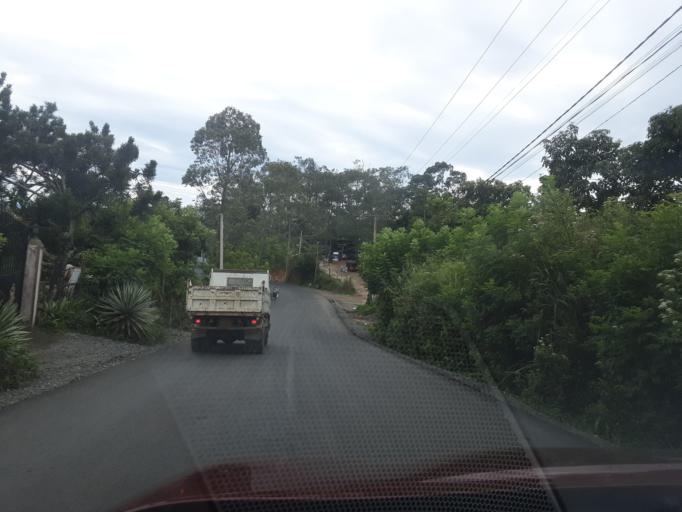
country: LK
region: Uva
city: Haputale
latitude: 6.8363
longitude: 80.9992
